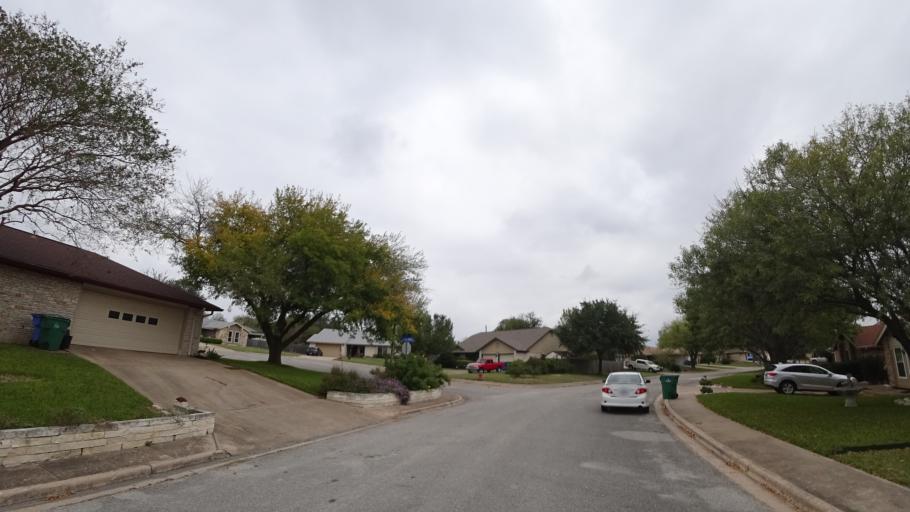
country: US
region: Texas
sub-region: Travis County
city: Pflugerville
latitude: 30.4294
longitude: -97.6094
